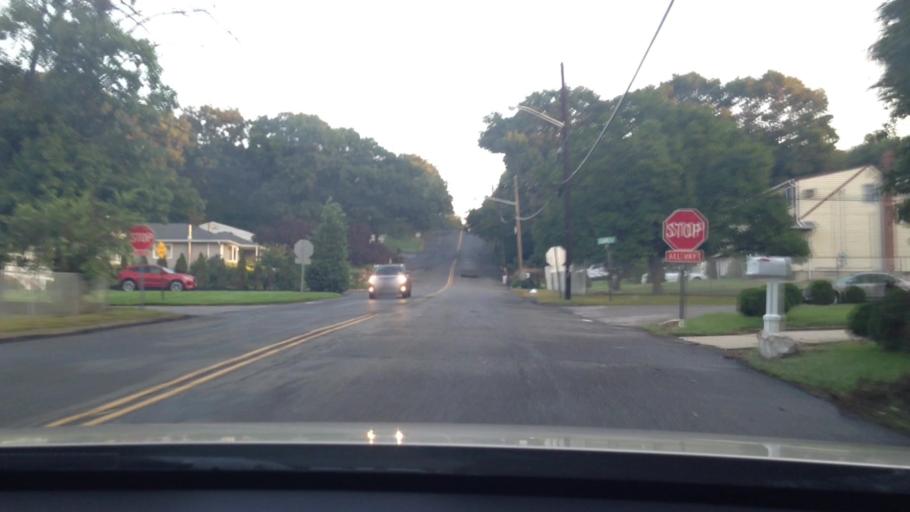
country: US
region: New York
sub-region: Suffolk County
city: Farmingville
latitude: 40.8374
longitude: -73.0347
